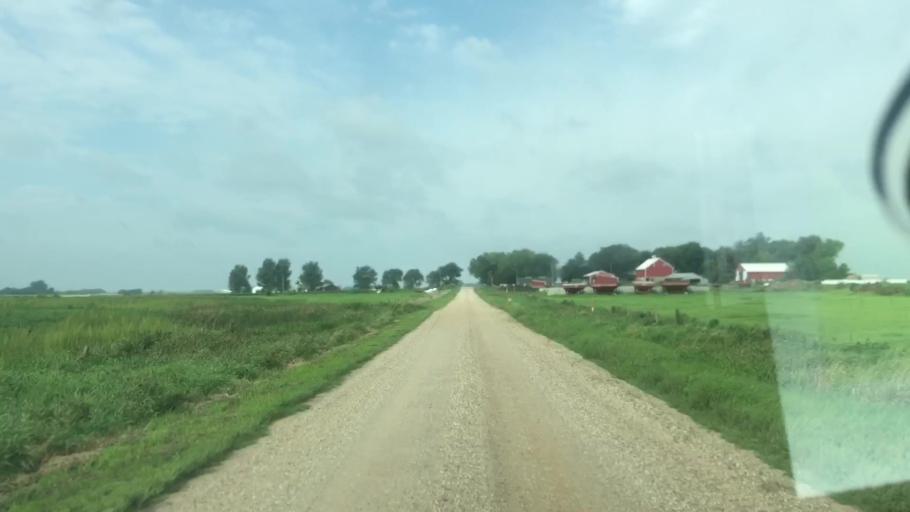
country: US
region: Iowa
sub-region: O'Brien County
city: Sheldon
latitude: 43.2724
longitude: -95.9148
